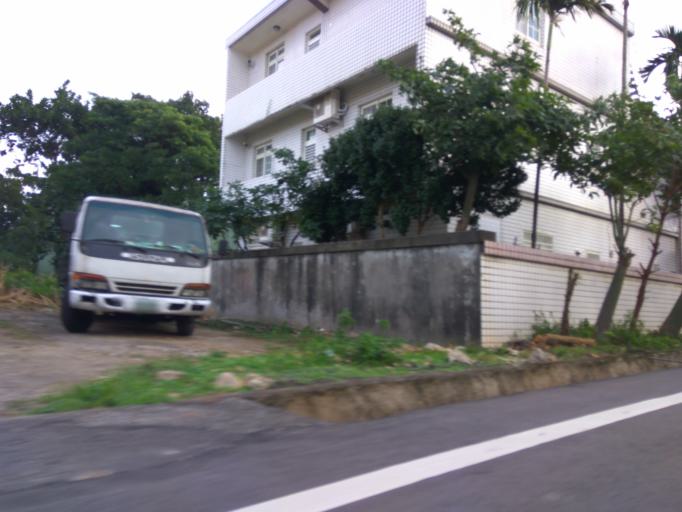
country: TW
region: Taiwan
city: Daxi
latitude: 24.9327
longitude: 121.1928
